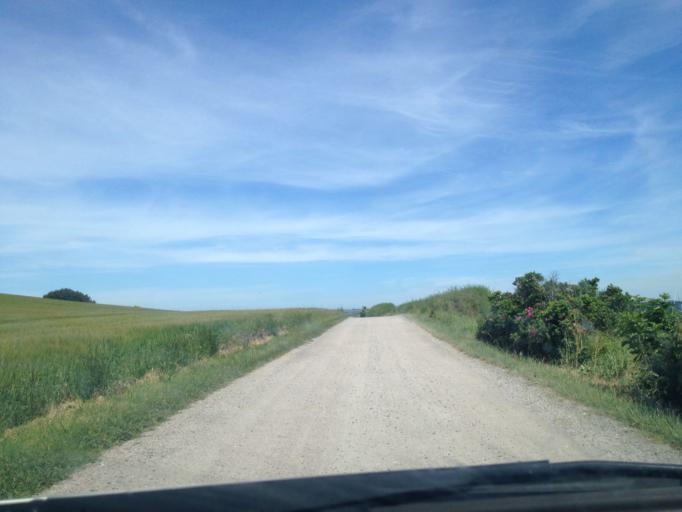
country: DK
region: Central Jutland
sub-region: Samso Kommune
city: Tranebjerg
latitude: 55.8805
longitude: 10.6771
